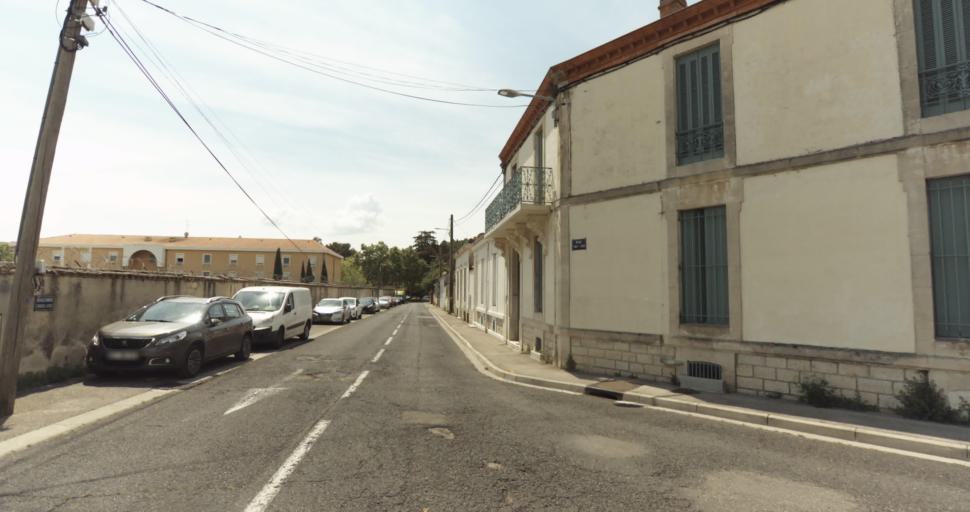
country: FR
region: Languedoc-Roussillon
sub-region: Departement du Gard
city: Nimes
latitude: 43.8480
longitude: 4.3681
